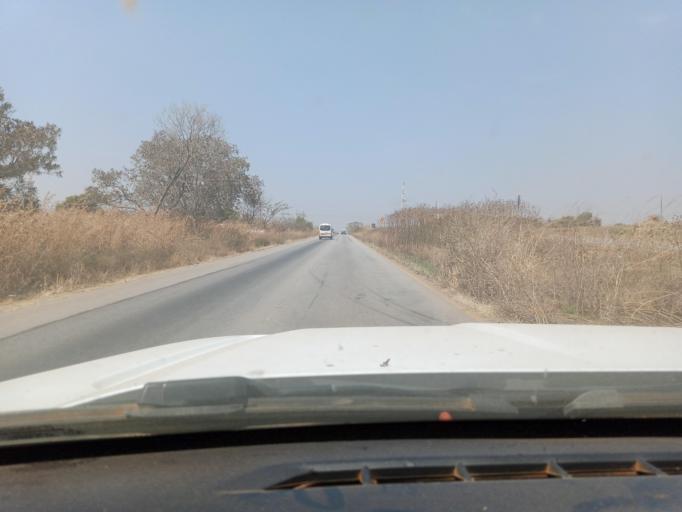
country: ZM
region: Copperbelt
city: Luanshya
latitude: -12.9713
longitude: 28.4001
